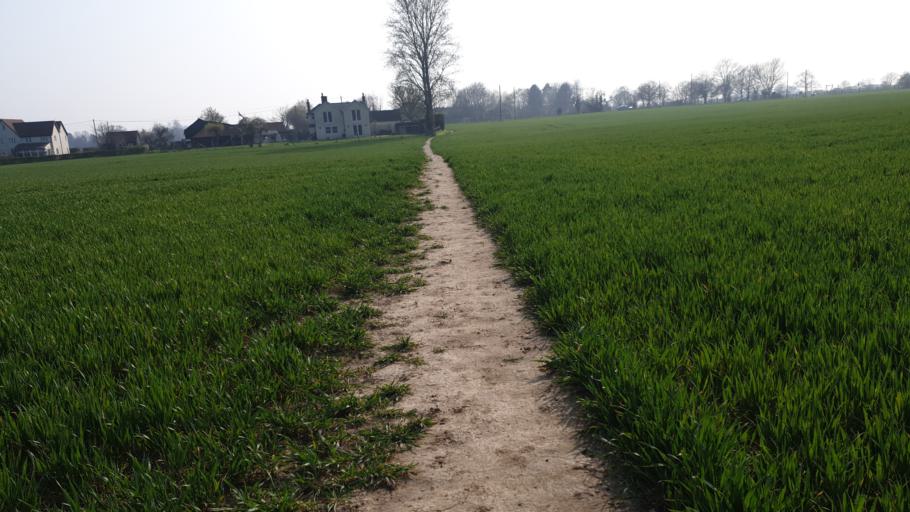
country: GB
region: England
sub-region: Essex
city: Great Bentley
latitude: 51.8832
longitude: 1.1179
